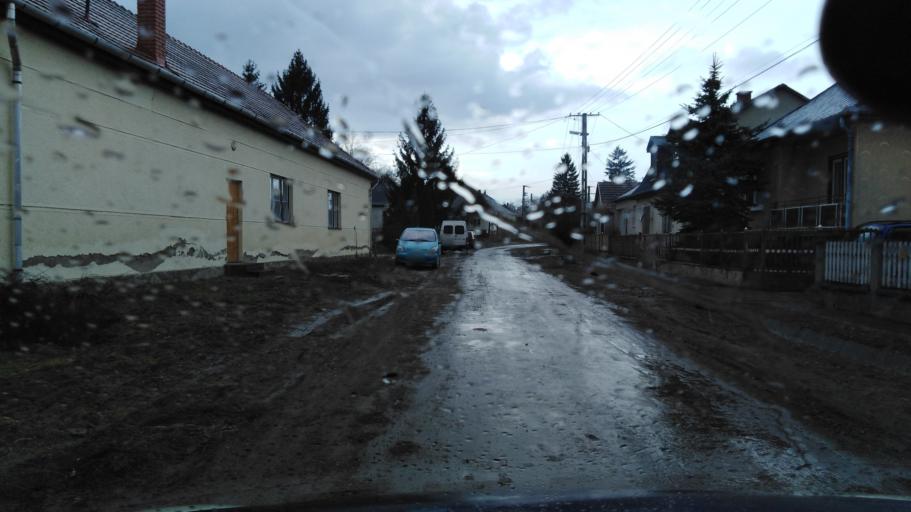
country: HU
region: Nograd
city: Karancskeszi
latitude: 48.1821
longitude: 19.6413
